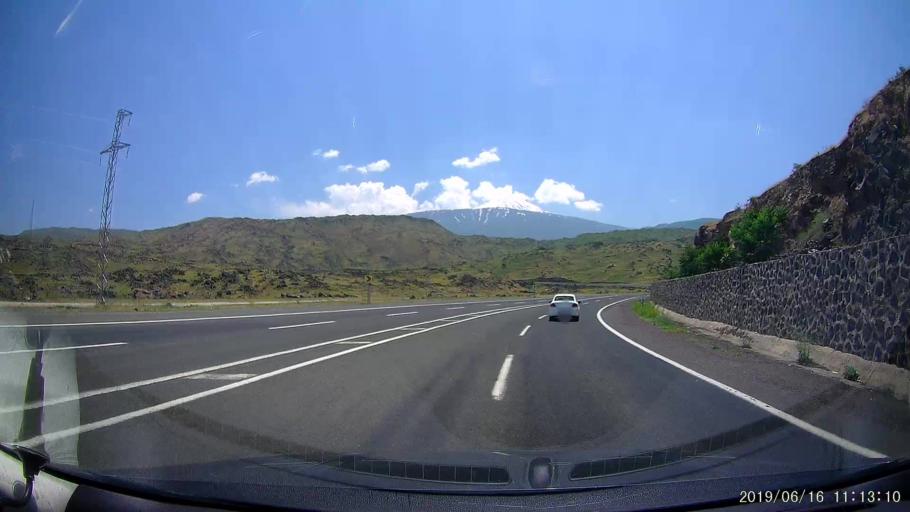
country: TR
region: Igdir
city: Igdir
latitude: 39.7873
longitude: 44.1345
